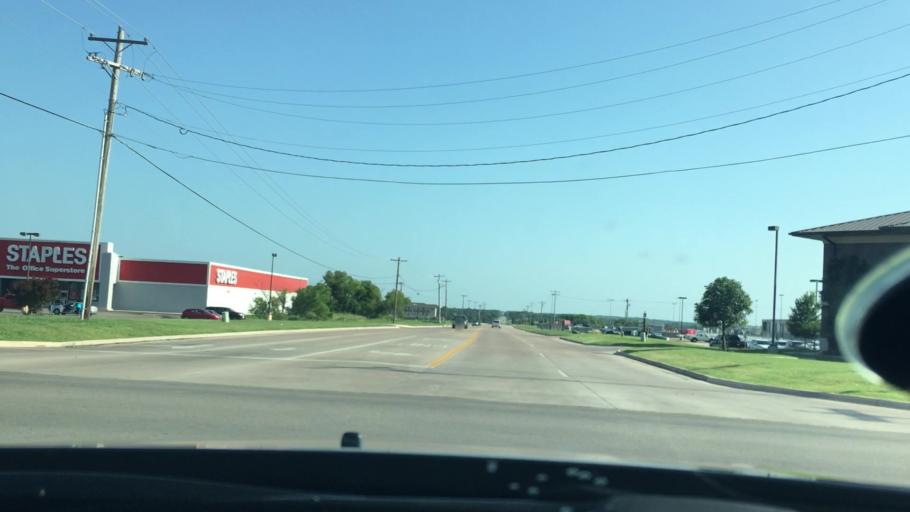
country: US
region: Oklahoma
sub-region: Pontotoc County
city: Ada
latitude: 34.7904
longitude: -96.6523
